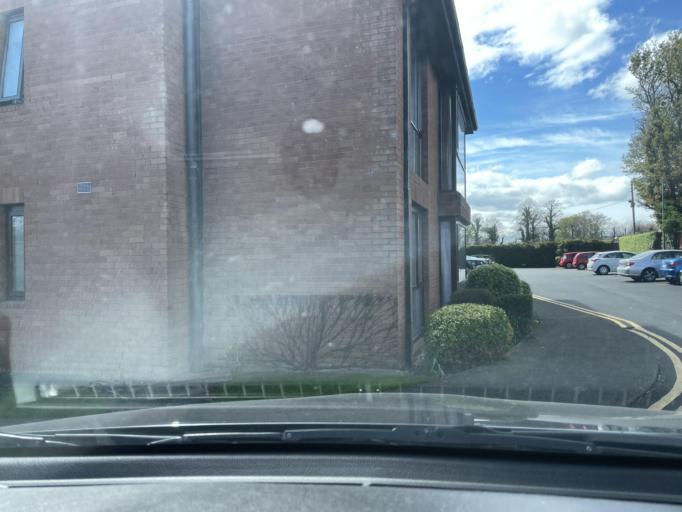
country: IE
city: Killester
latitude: 53.3762
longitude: -6.1998
